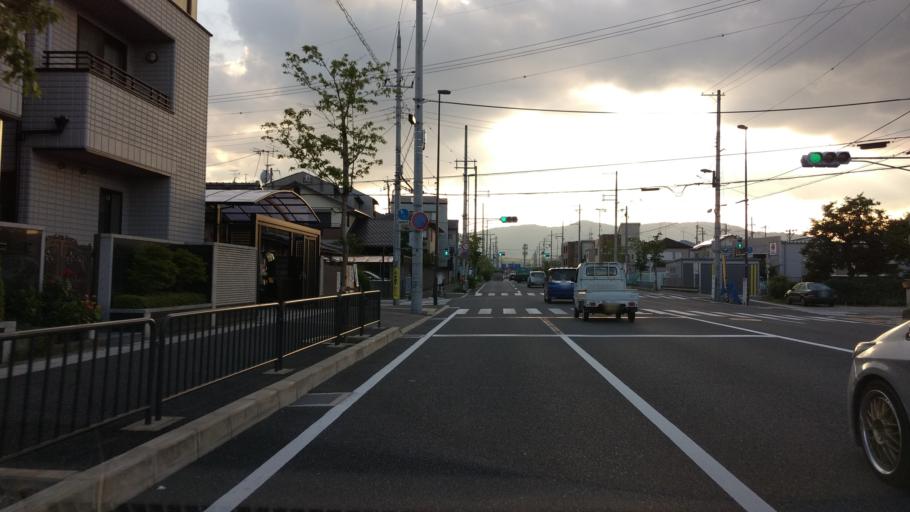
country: JP
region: Kyoto
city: Muko
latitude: 34.9547
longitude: 135.7212
